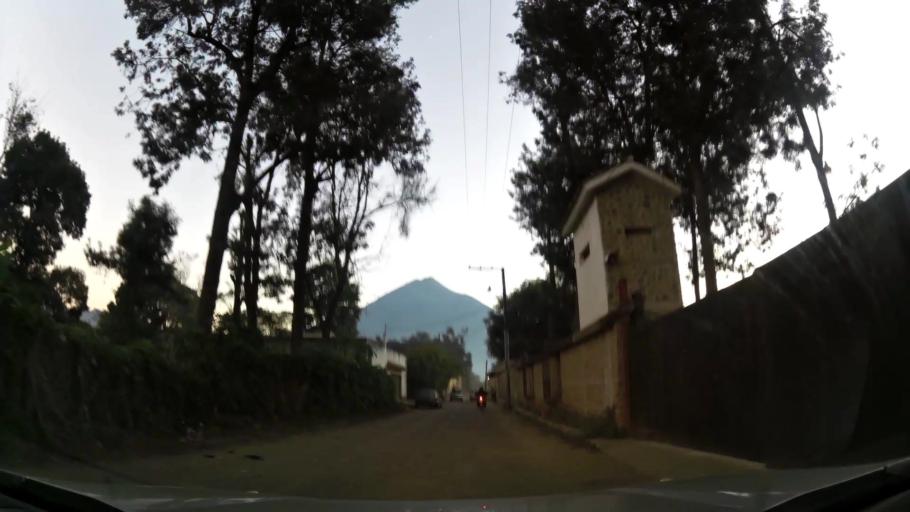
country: GT
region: Sacatepequez
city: Antigua Guatemala
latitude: 14.5462
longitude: -90.7480
